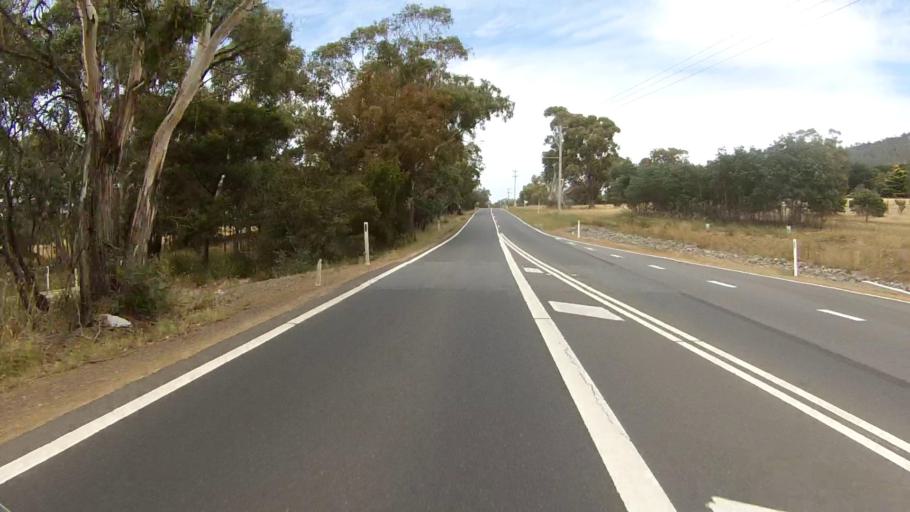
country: AU
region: Tasmania
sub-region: Clarence
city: Acton Park
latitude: -42.8850
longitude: 147.4832
